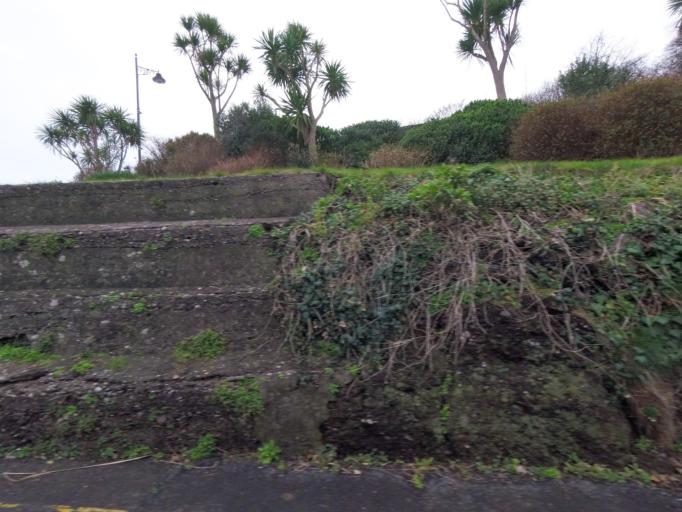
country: IE
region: Munster
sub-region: Waterford
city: Dunmore East
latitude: 52.1539
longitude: -6.9943
